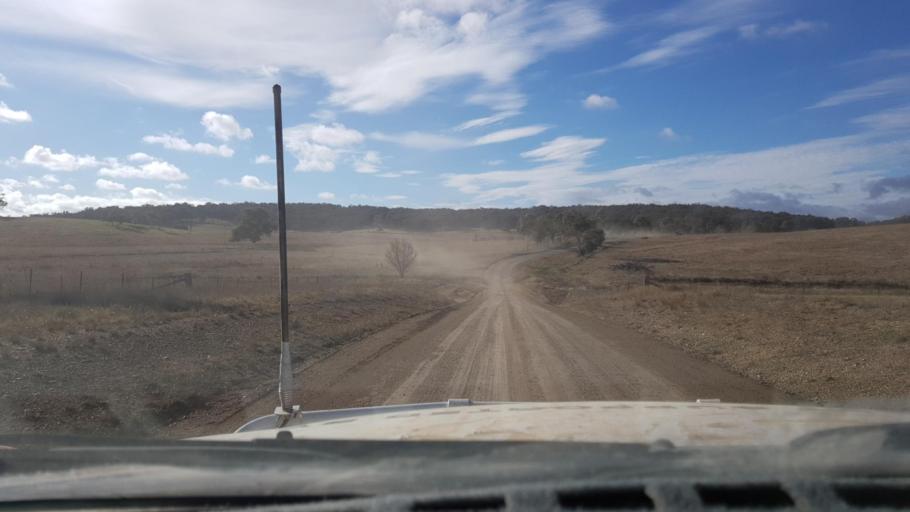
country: AU
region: New South Wales
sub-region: Armidale Dumaresq
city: Enmore
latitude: -30.7465
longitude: 151.6162
